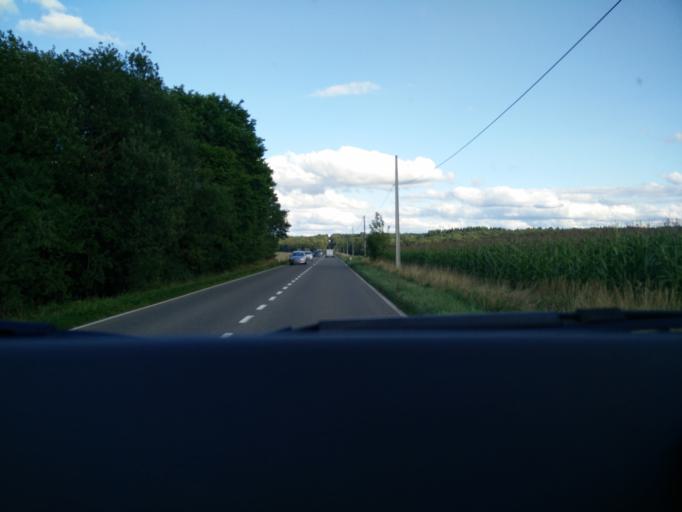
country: BE
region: Wallonia
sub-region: Province de Namur
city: Walcourt
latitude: 50.2103
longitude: 4.4655
